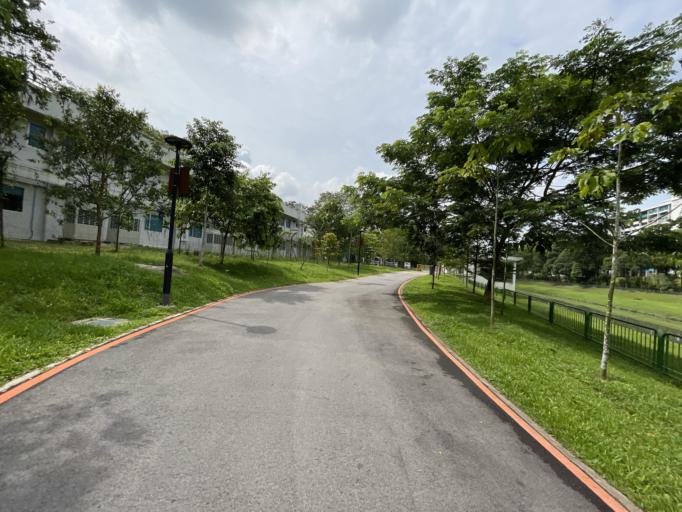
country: SG
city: Singapore
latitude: 1.3213
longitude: 103.7690
